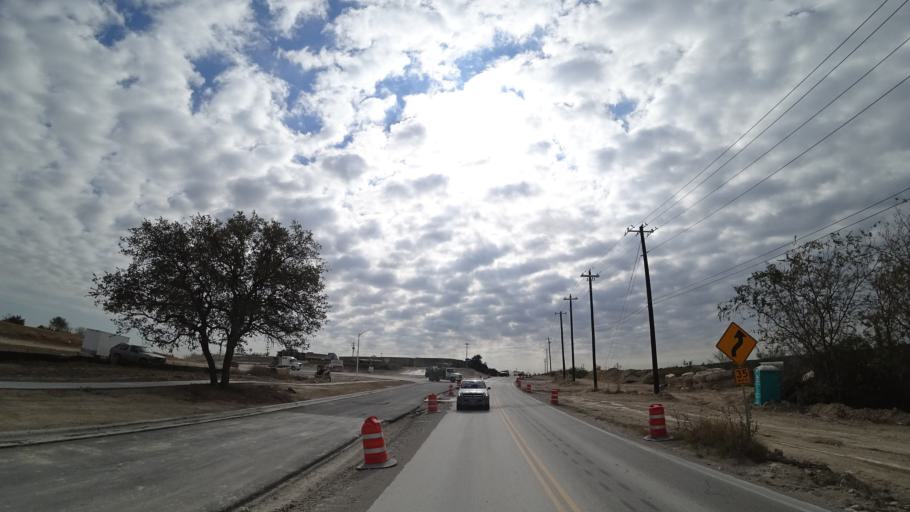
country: US
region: Texas
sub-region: Williamson County
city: Cedar Park
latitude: 30.5083
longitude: -97.8569
